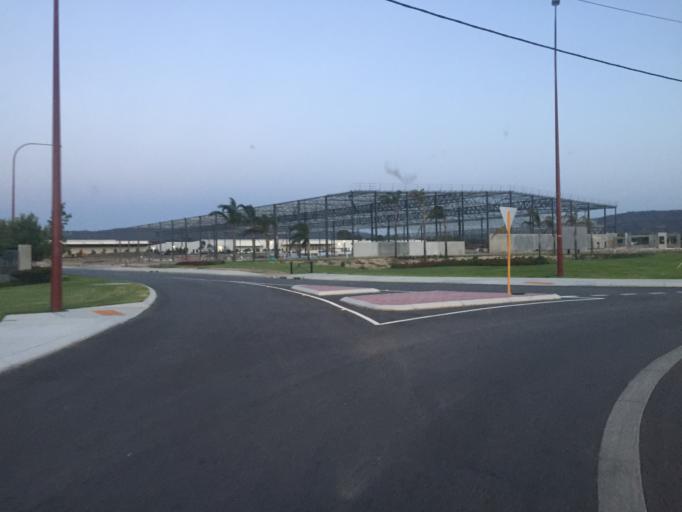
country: AU
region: Western Australia
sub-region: Gosnells
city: Maddington
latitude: -32.0320
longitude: 115.9962
